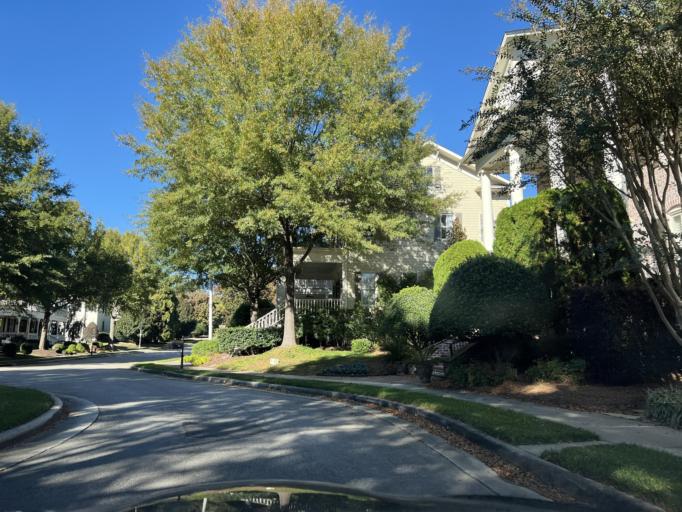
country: US
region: North Carolina
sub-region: Wake County
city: West Raleigh
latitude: 35.8949
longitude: -78.6454
